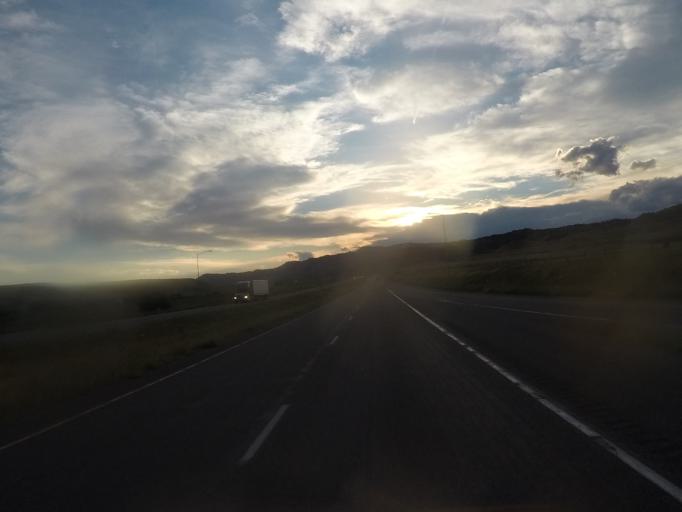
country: US
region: Montana
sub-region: Park County
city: Livingston
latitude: 45.6522
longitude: -110.6146
